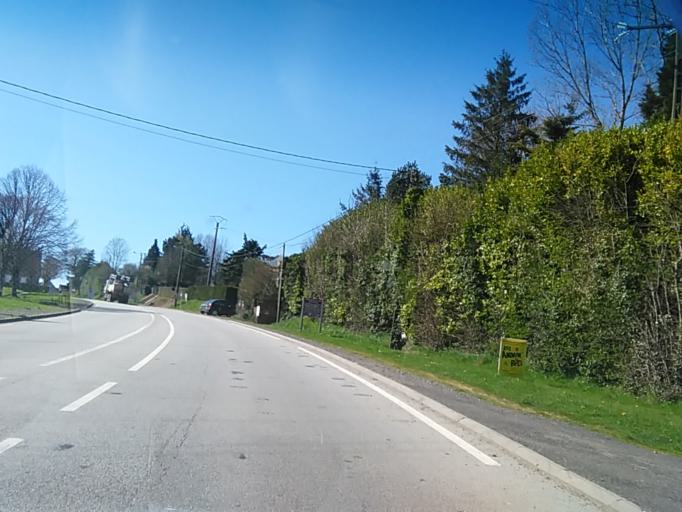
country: FR
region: Pays de la Loire
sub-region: Departement de la Mayenne
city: Pre-en-Pail
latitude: 48.5658
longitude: -0.1395
